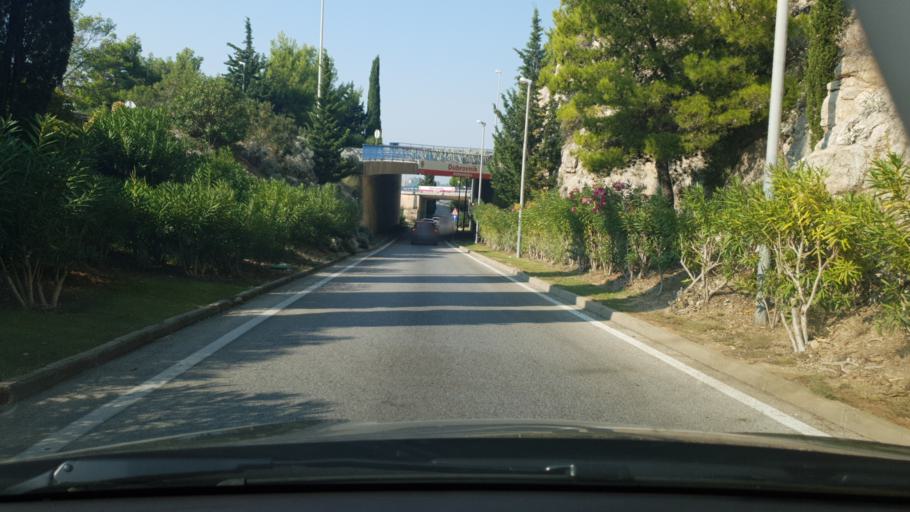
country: HR
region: Dubrovacko-Neretvanska
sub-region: Grad Dubrovnik
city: Dubrovnik
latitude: 42.6454
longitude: 18.1097
